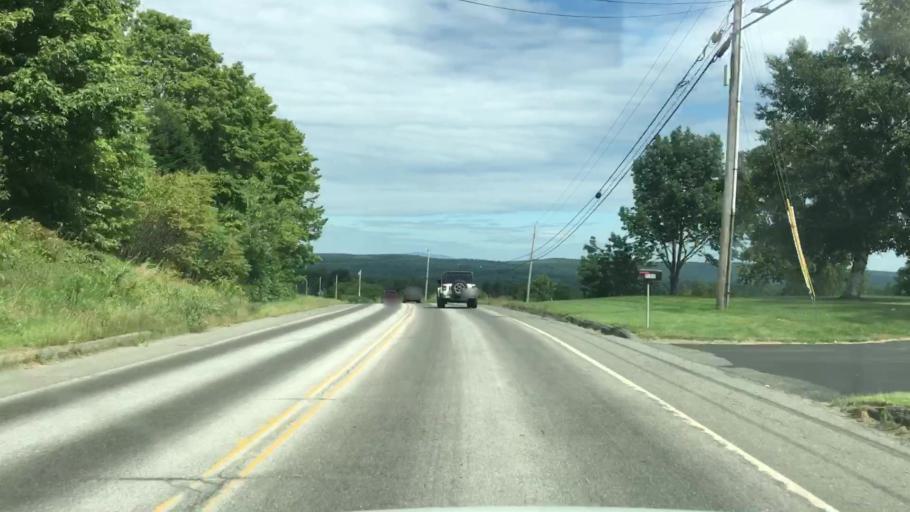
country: US
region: Maine
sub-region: Piscataquis County
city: Dover-Foxcroft
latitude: 45.1640
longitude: -69.2308
